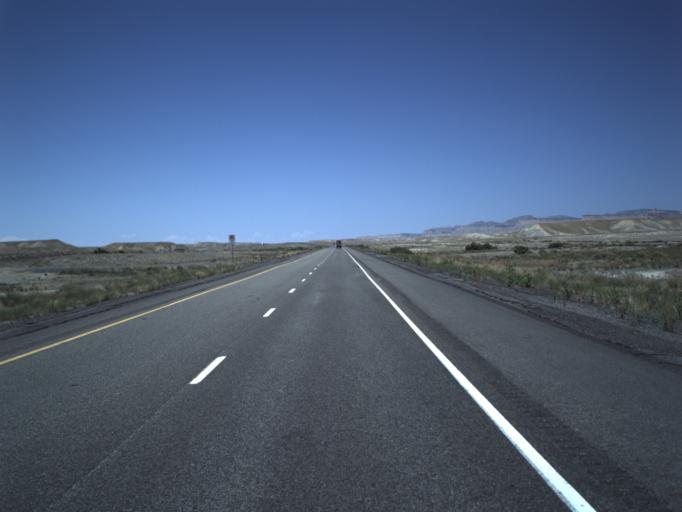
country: US
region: Utah
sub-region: Grand County
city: Moab
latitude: 38.9405
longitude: -109.5069
